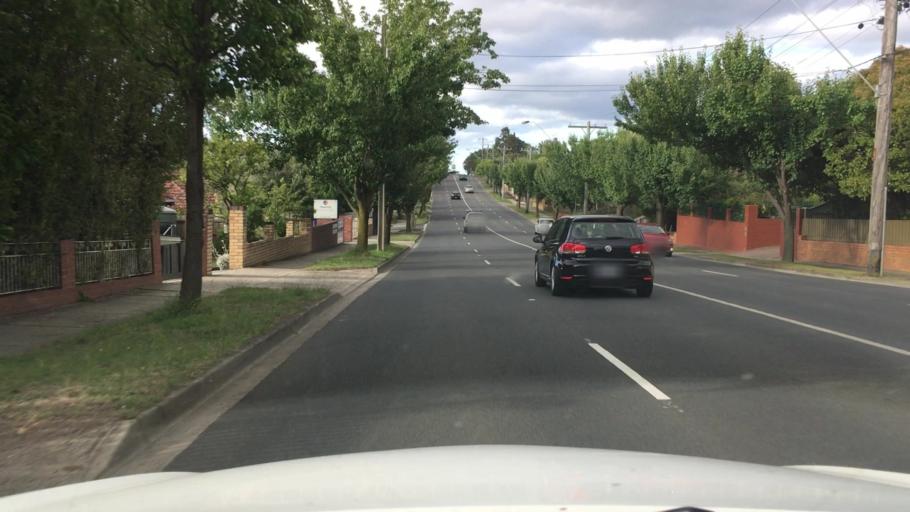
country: AU
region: Victoria
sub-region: Whitehorse
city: Burwood
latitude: -37.8559
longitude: 145.1317
